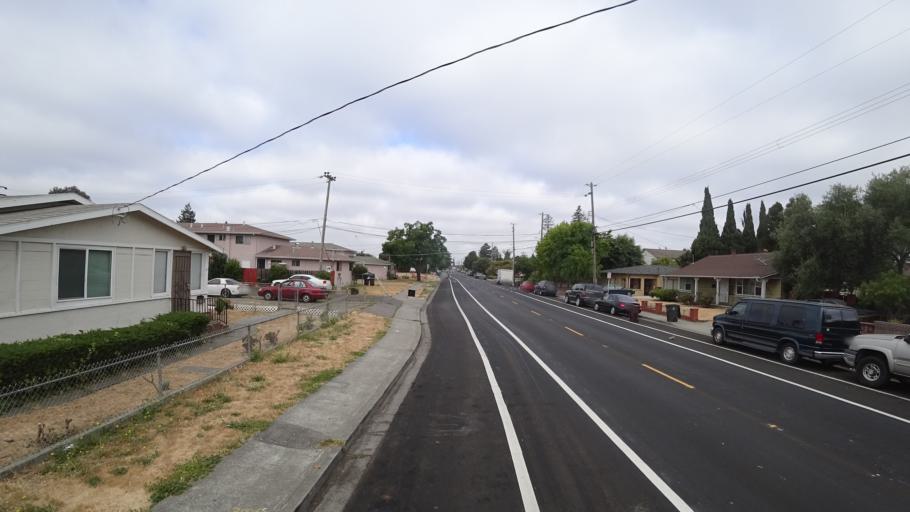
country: US
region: California
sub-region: Alameda County
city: Hayward
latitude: 37.6409
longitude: -122.0746
